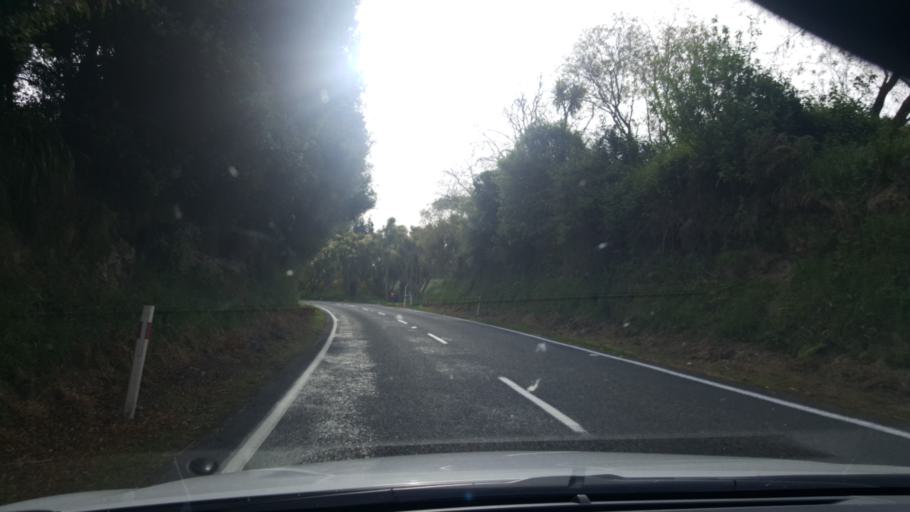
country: NZ
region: Waikato
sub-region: Taupo District
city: Taupo
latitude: -38.6129
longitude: 176.1260
